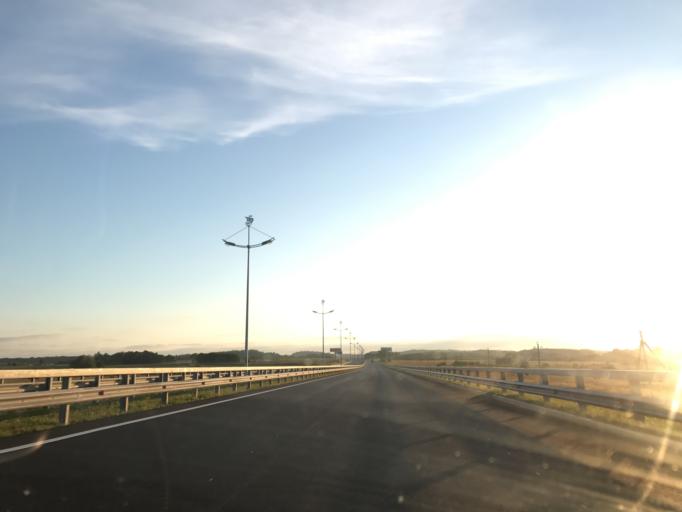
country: RU
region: Kaliningrad
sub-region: Gorod Kaliningrad
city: Pionerskiy
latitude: 54.9216
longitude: 20.3234
